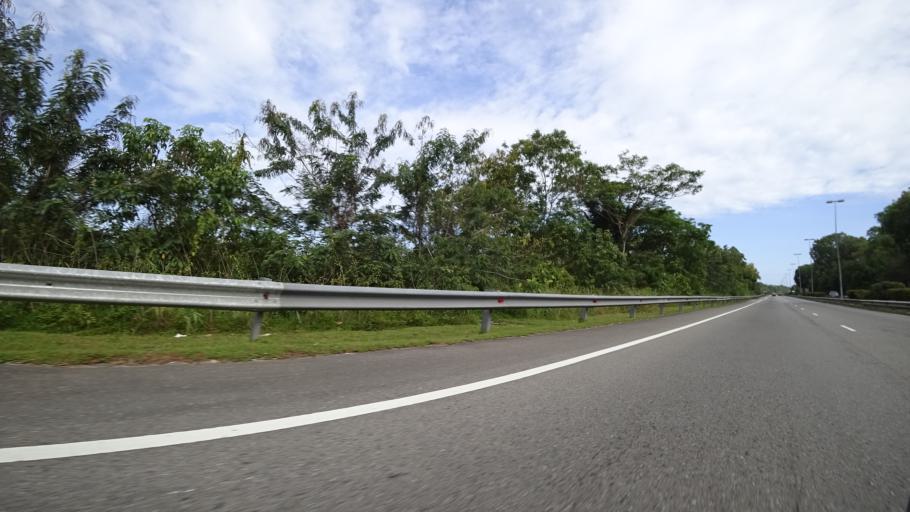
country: BN
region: Brunei and Muara
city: Bandar Seri Begawan
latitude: 4.9292
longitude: 114.9117
